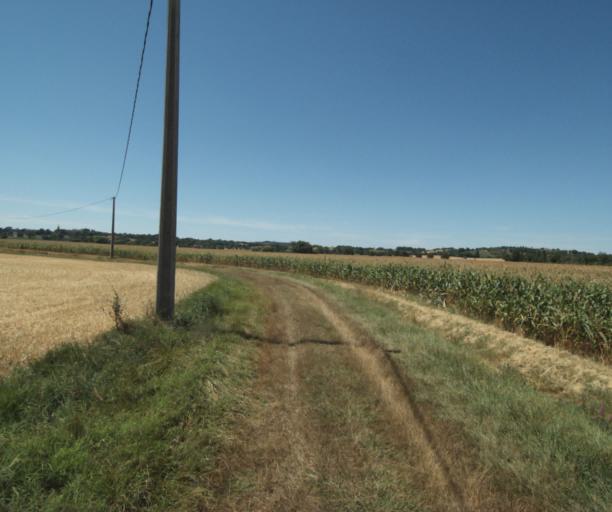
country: FR
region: Midi-Pyrenees
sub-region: Departement de la Haute-Garonne
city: Saint-Felix-Lauragais
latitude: 43.4825
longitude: 1.9427
